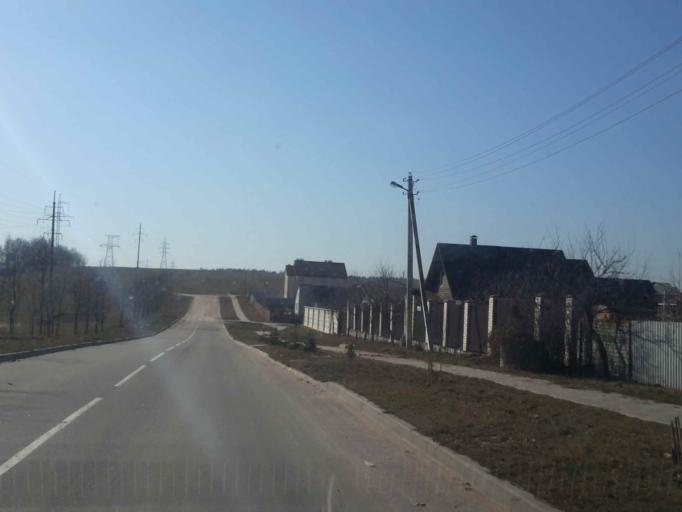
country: BY
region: Minsk
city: Zhdanovichy
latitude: 53.9190
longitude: 27.4113
